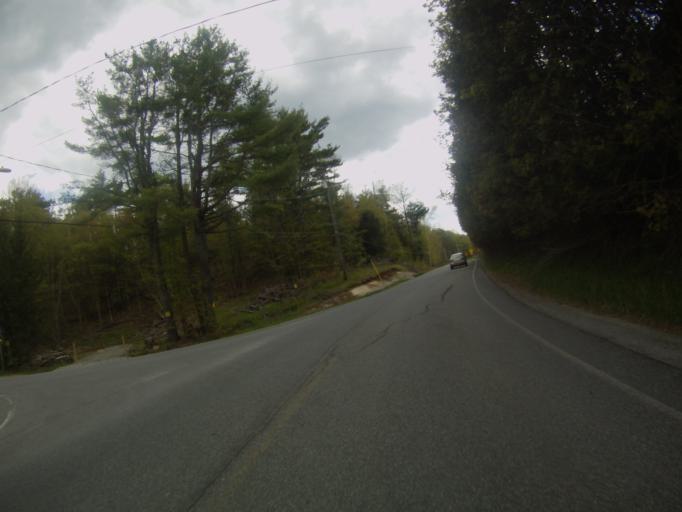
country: US
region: New York
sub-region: Essex County
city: Mineville
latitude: 44.0416
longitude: -73.5593
